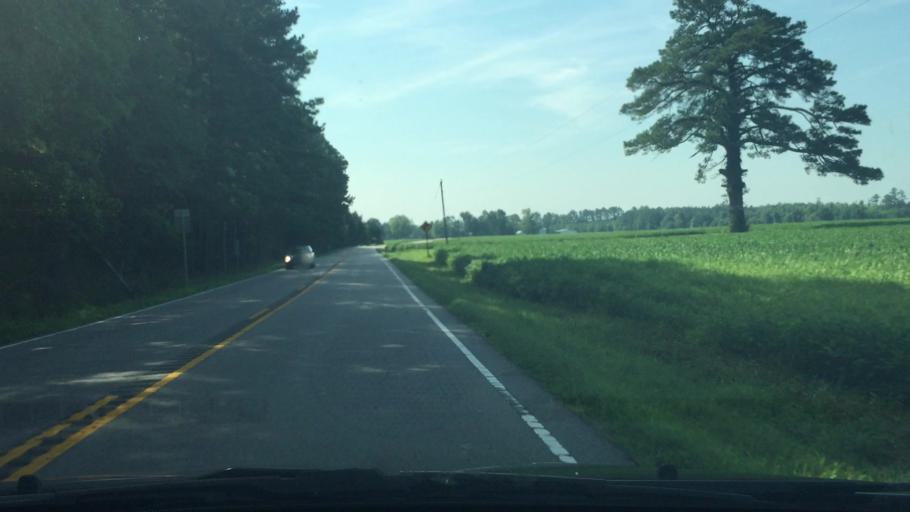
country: US
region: Virginia
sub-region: Southampton County
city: Courtland
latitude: 36.8489
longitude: -77.1333
